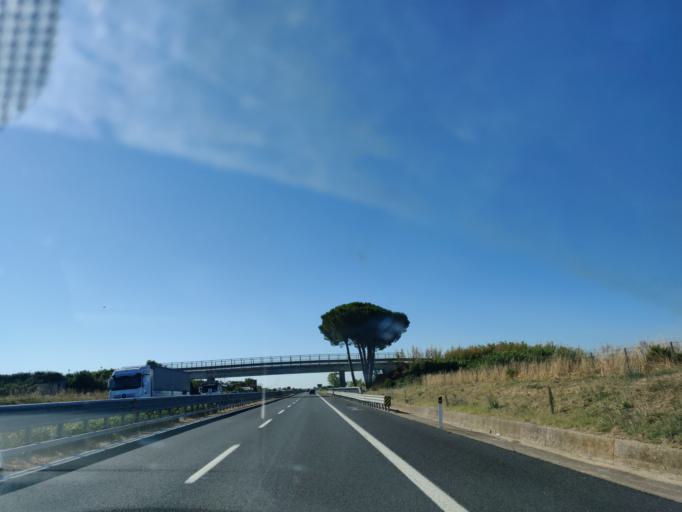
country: IT
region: Latium
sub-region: Citta metropolitana di Roma Capitale
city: Marina San Nicola
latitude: 41.9552
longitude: 12.1292
